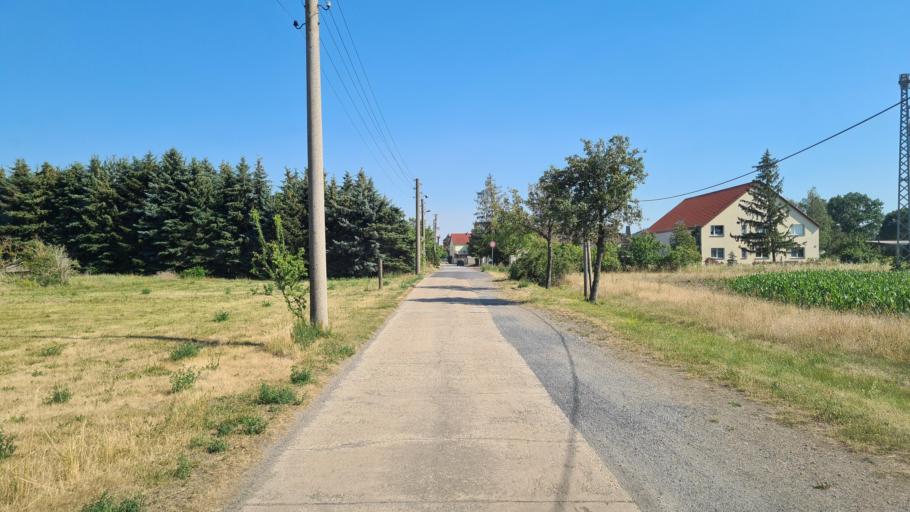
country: DE
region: Saxony-Anhalt
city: Annaburg
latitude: 51.7006
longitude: 12.9911
